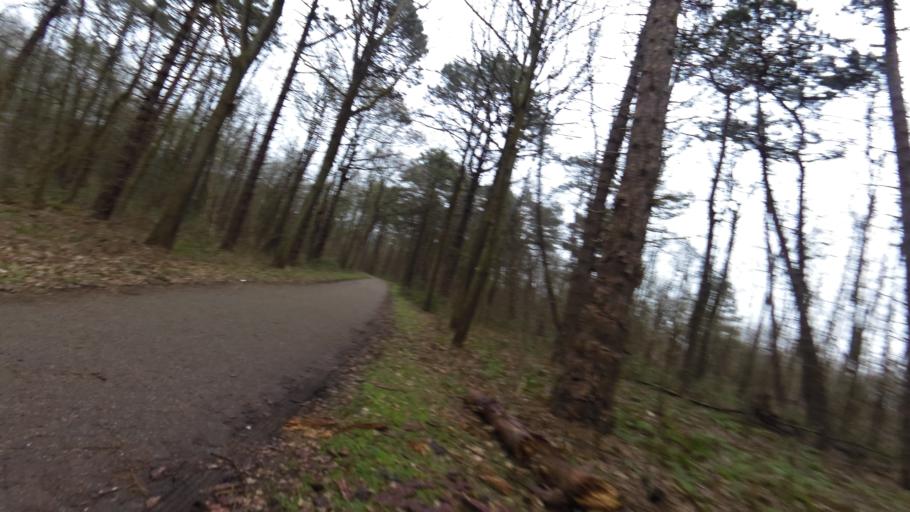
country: NL
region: North Holland
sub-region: Gemeente Castricum
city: Castricum
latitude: 52.5545
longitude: 4.6242
